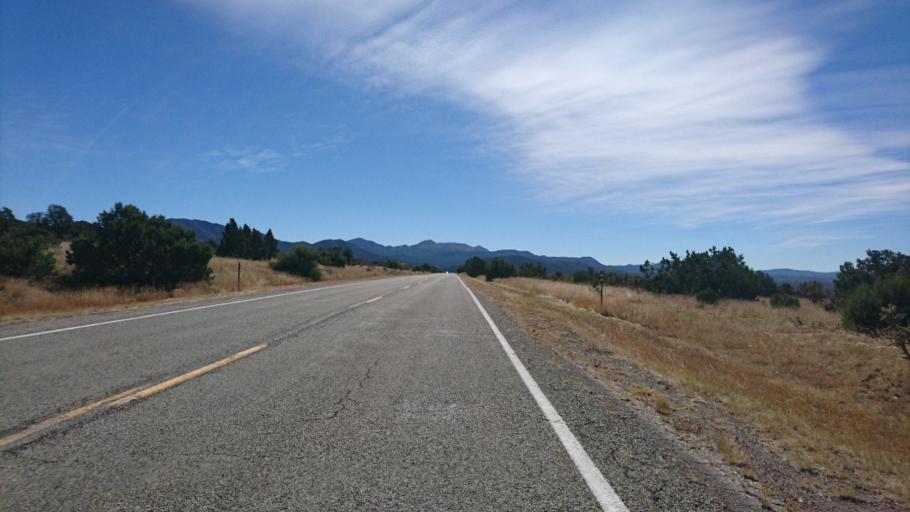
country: US
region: New Mexico
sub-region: Bernalillo County
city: Sandia Knolls
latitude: 35.3046
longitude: -106.2156
